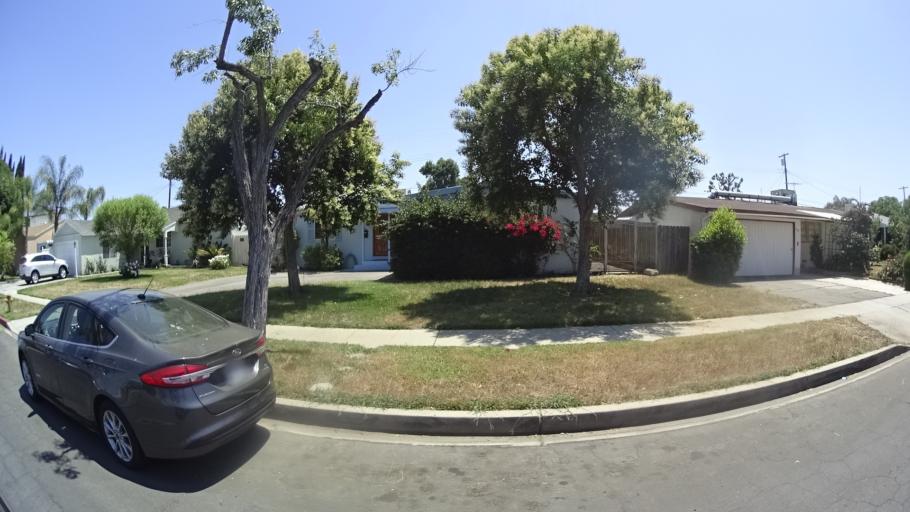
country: US
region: California
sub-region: Los Angeles County
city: Van Nuys
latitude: 34.2118
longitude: -118.4326
